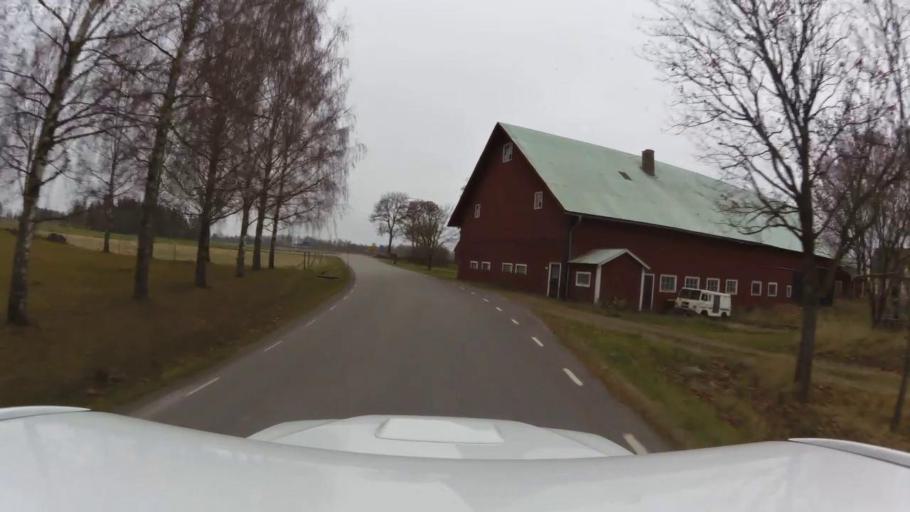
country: SE
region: OEstergoetland
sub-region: Linkopings Kommun
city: Vikingstad
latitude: 58.3208
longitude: 15.3761
